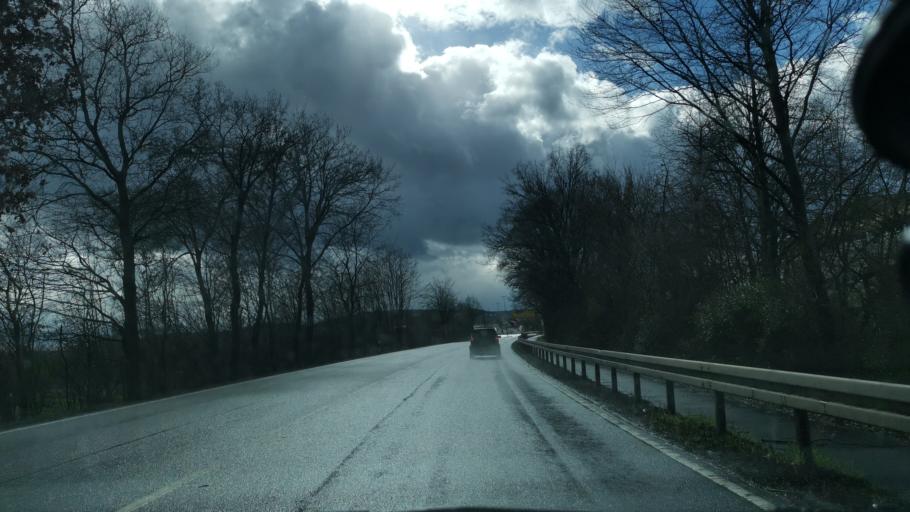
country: DE
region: Hesse
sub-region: Regierungsbezirk Kassel
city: Bad Hersfeld
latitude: 50.8680
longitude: 9.7233
